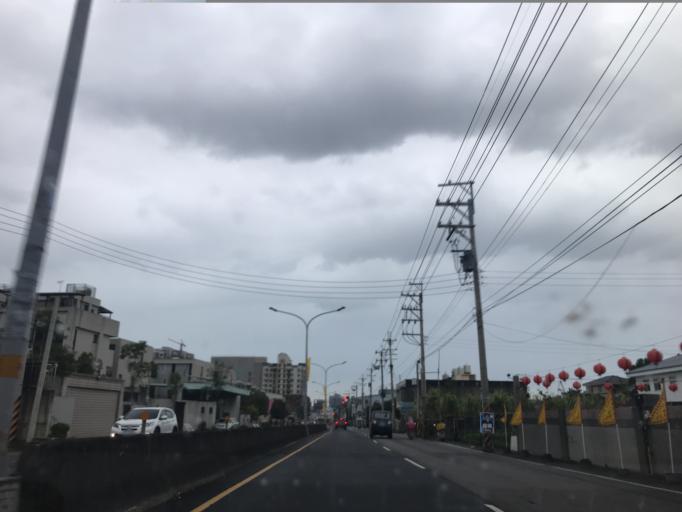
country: TW
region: Taiwan
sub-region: Hsinchu
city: Zhubei
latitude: 24.8315
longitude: 121.0322
